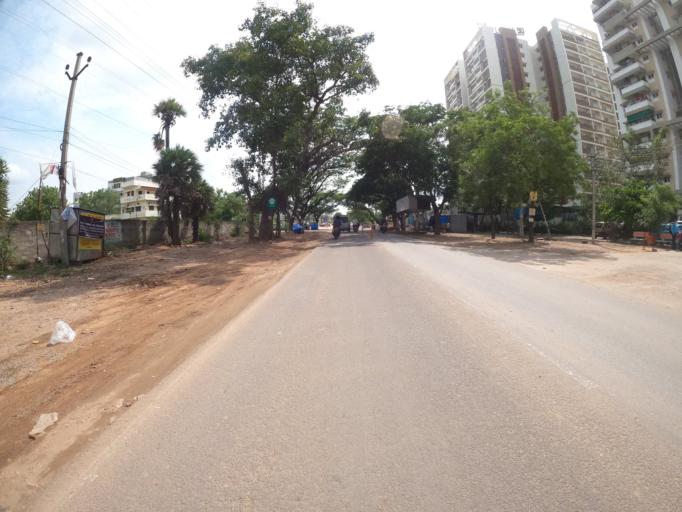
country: IN
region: Telangana
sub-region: Medak
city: Serilingampalle
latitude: 17.3873
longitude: 78.3395
